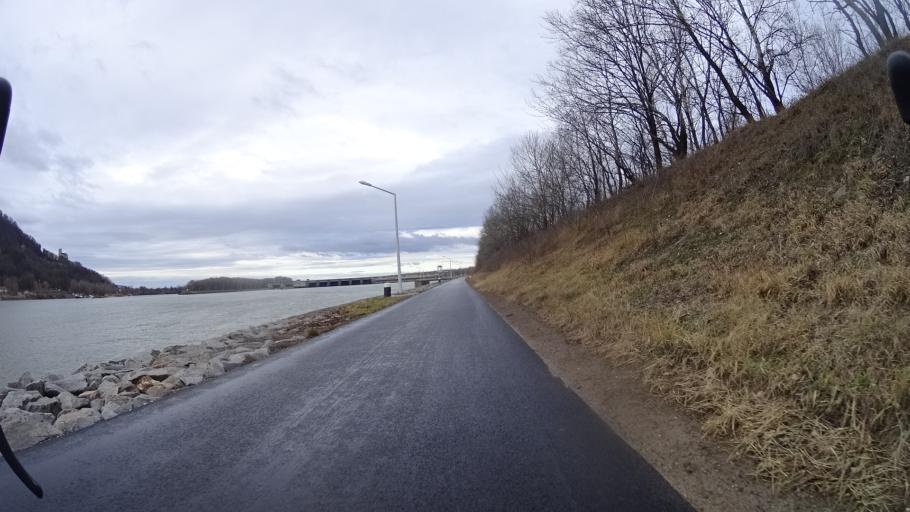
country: AT
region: Lower Austria
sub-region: Politischer Bezirk Korneuburg
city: Spillern
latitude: 48.3553
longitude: 16.2581
